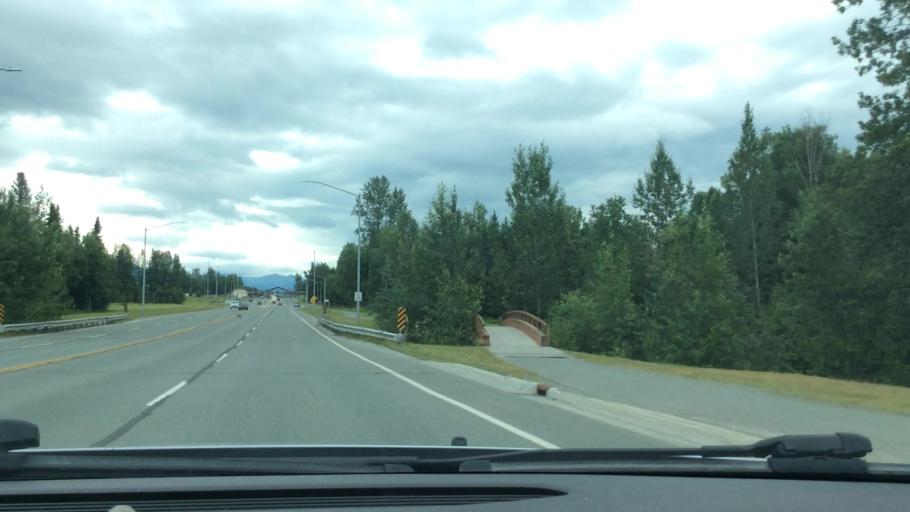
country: US
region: Alaska
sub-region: Anchorage Municipality
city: Anchorage
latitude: 61.2378
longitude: -149.7786
